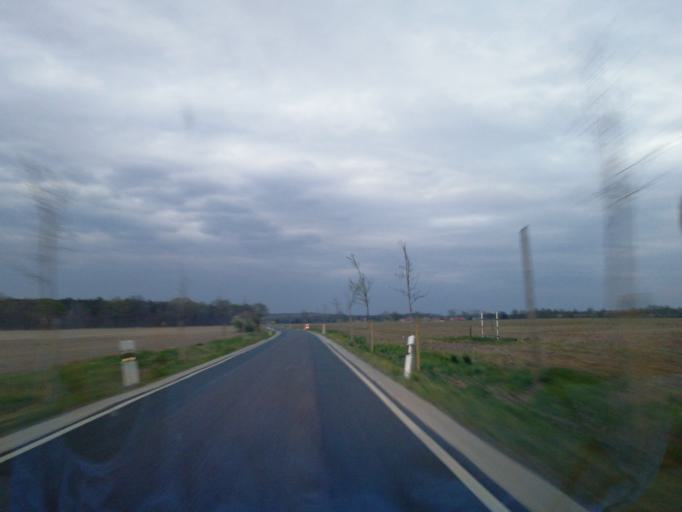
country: DE
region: Brandenburg
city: Calau
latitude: 51.7672
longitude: 13.8980
